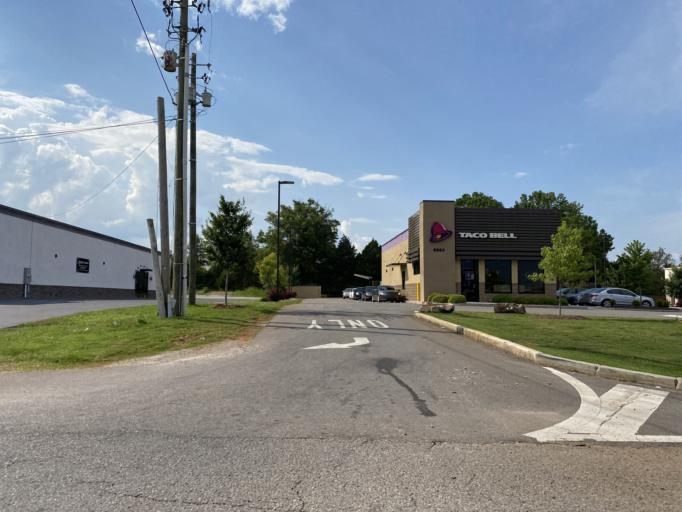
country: US
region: Alabama
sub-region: Madison County
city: Madison
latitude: 34.6776
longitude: -86.7498
